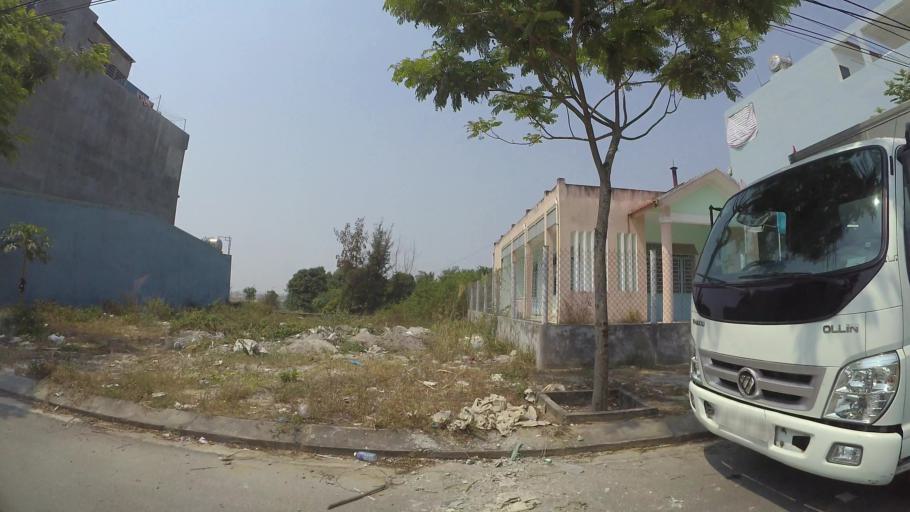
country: VN
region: Da Nang
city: Ngu Hanh Son
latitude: 16.0154
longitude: 108.2507
